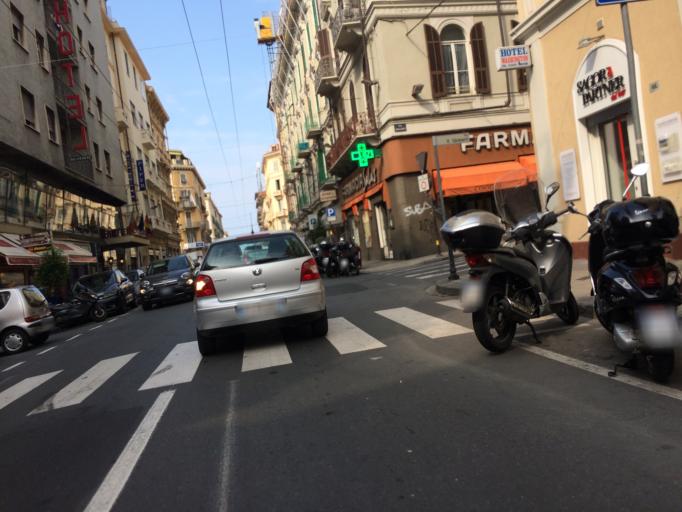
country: IT
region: Liguria
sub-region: Provincia di Imperia
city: San Remo
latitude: 43.8164
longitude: 7.7770
